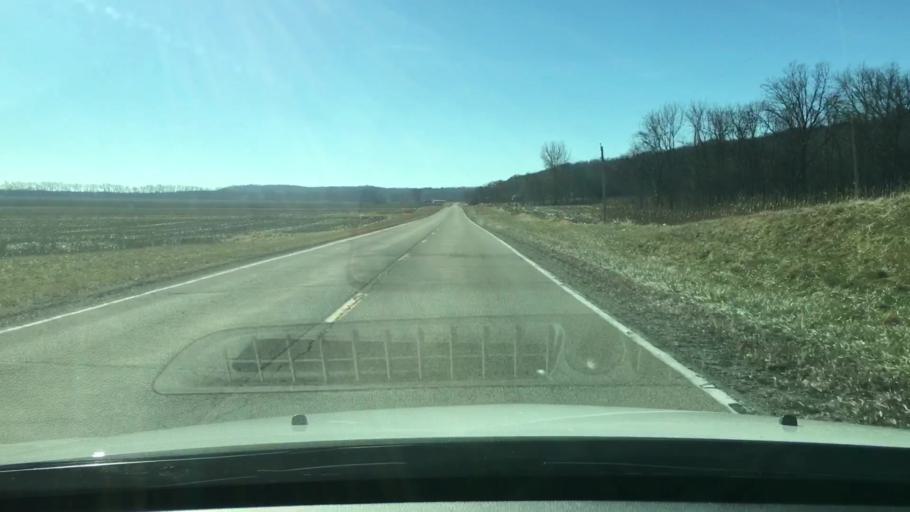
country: US
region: Illinois
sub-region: Mason County
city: Havana
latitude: 40.2447
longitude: -90.1892
